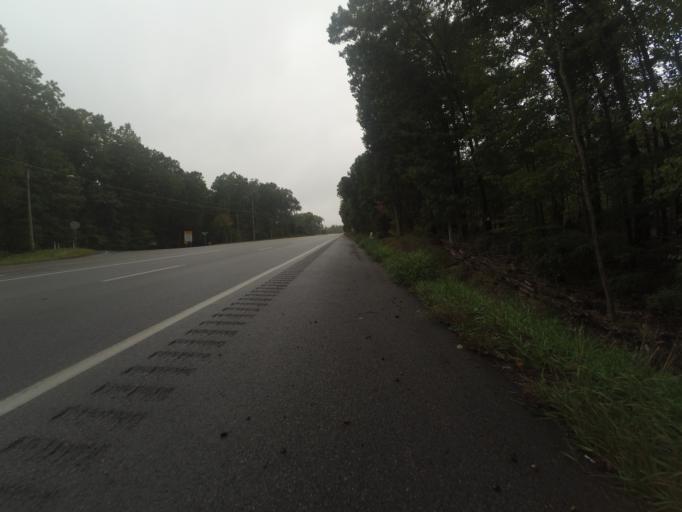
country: US
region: Pennsylvania
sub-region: Huntingdon County
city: Huntingdon
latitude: 40.4984
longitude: -78.0578
